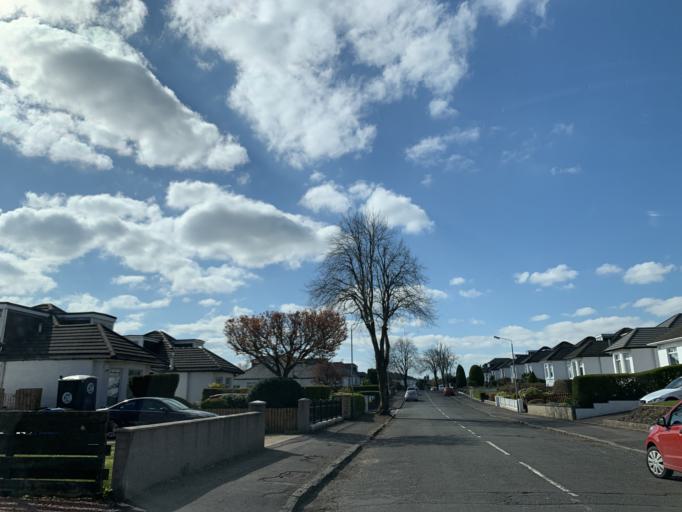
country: GB
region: Scotland
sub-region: East Renfrewshire
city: Clarkston
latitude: 55.7922
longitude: -4.2724
